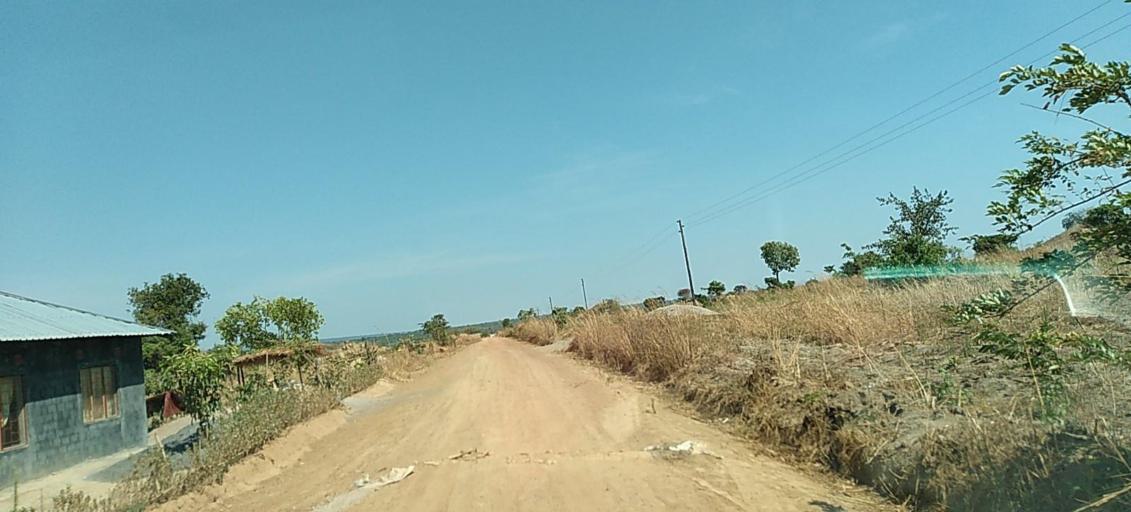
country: ZM
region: Copperbelt
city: Chililabombwe
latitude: -12.3433
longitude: 27.8727
